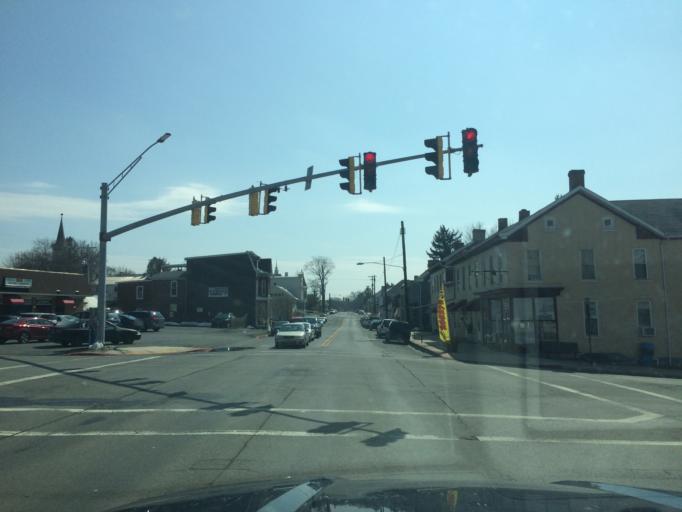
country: US
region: Maryland
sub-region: Washington County
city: Williamsport
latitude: 39.5994
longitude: -77.8213
